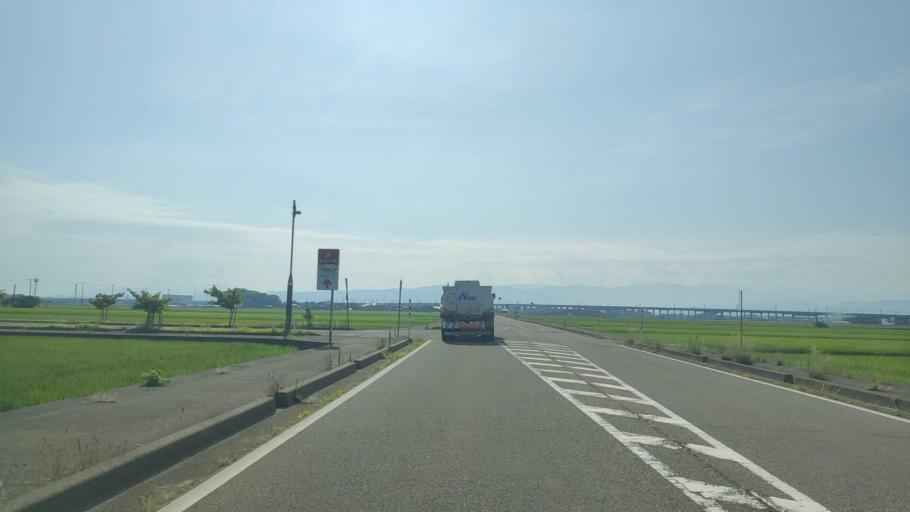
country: JP
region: Ishikawa
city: Matsuto
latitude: 36.5002
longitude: 136.5074
